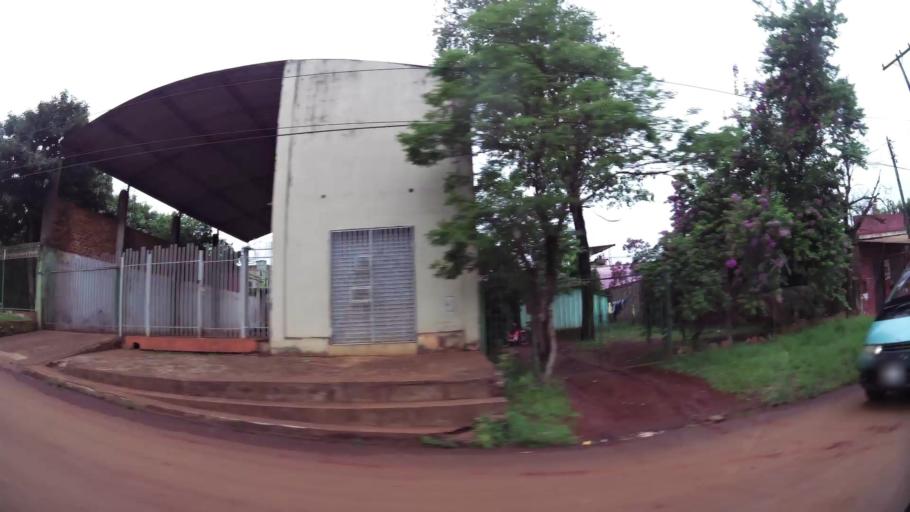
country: PY
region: Alto Parana
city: Ciudad del Este
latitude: -25.4980
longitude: -54.6876
